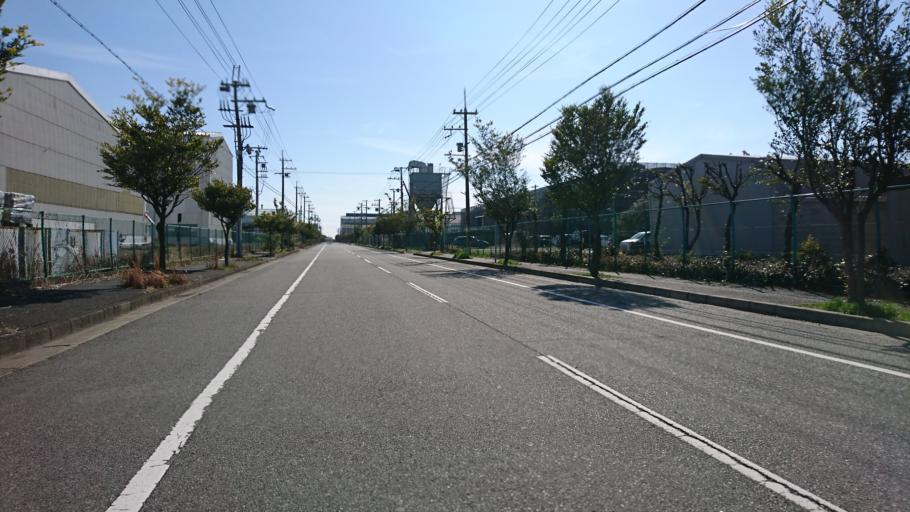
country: JP
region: Hyogo
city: Kakogawacho-honmachi
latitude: 34.7012
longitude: 134.8497
